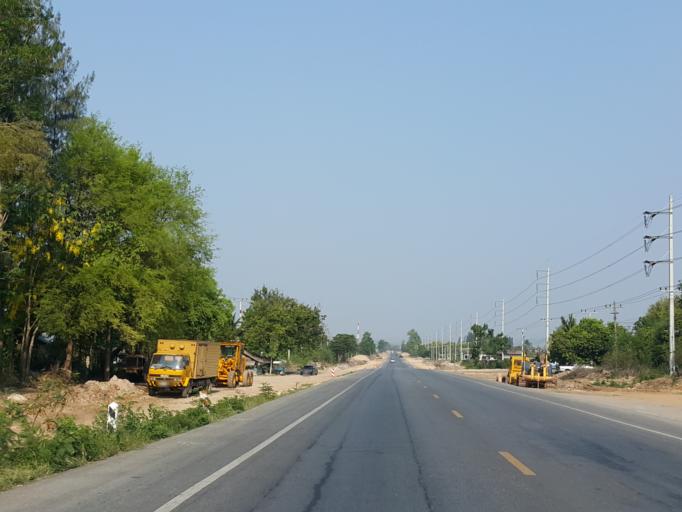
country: TH
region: Kanchanaburi
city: Sai Yok
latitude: 14.0873
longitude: 99.3382
